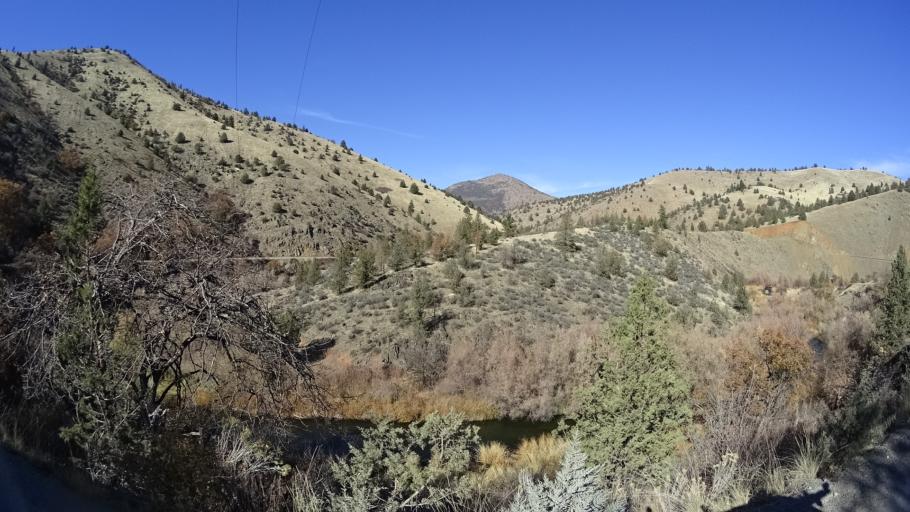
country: US
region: California
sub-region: Siskiyou County
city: Yreka
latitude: 41.7817
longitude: -122.6017
